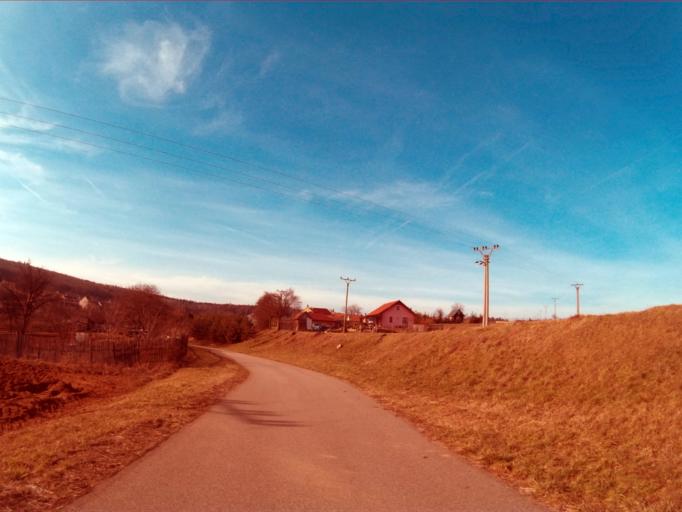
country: CZ
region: Vysocina
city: Mohelno
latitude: 49.1453
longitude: 16.1759
